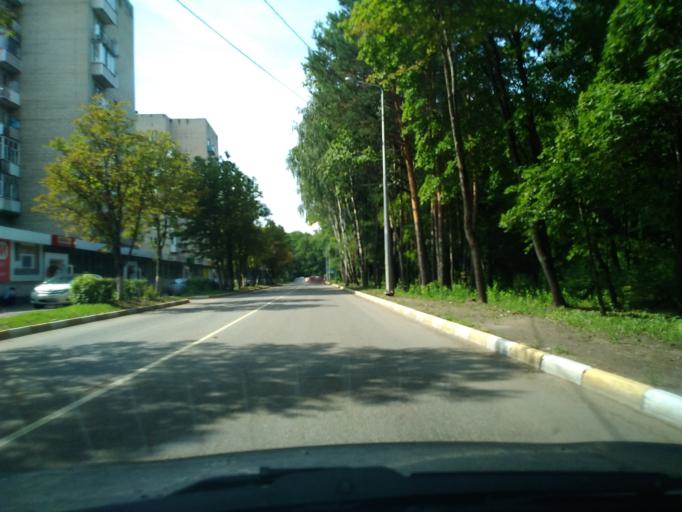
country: RU
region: Moskovskaya
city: Voskresensk
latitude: 55.3271
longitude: 38.6620
